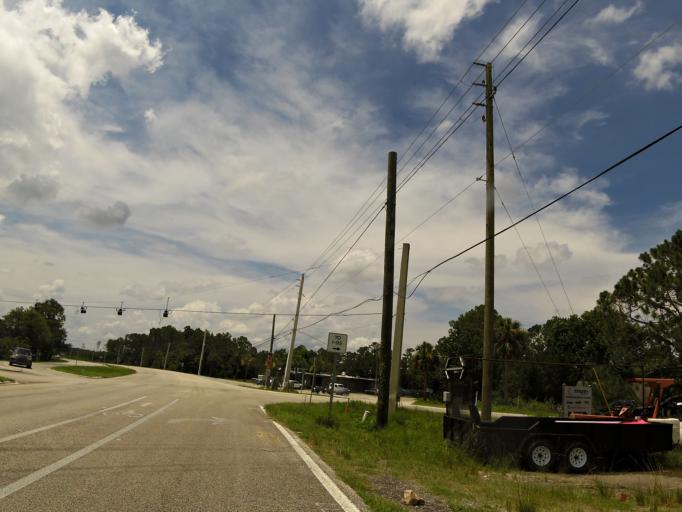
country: US
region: Florida
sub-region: Flagler County
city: Bunnell
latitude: 29.4067
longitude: -81.1965
